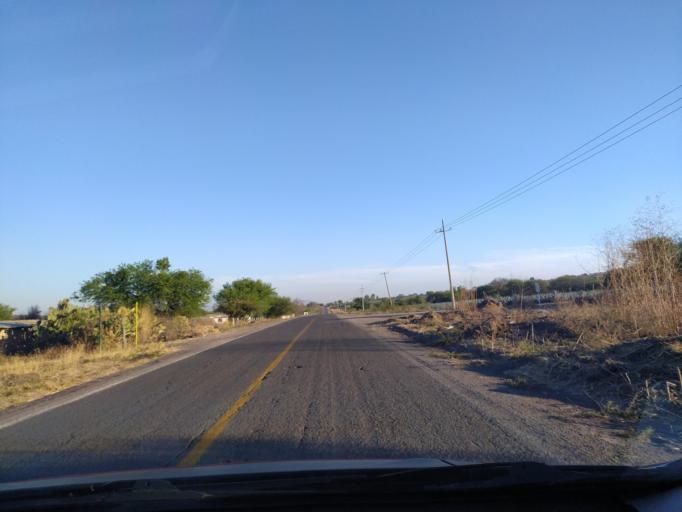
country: MX
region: Guanajuato
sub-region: San Francisco del Rincon
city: San Ignacio de Hidalgo
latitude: 20.8129
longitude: -101.8391
